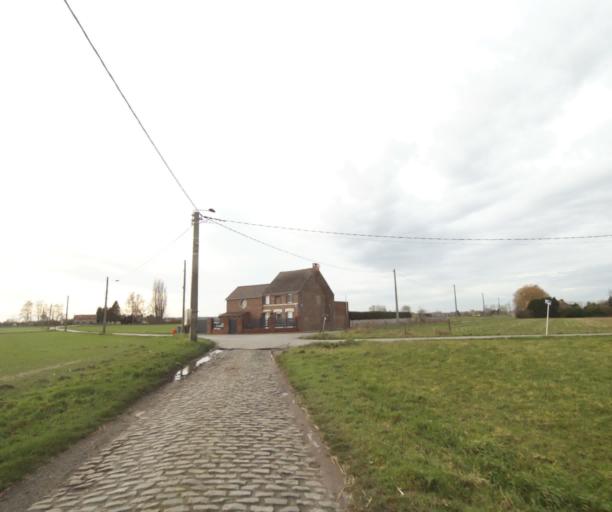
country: FR
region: Nord-Pas-de-Calais
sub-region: Departement du Nord
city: Hergnies
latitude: 50.4870
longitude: 3.5495
